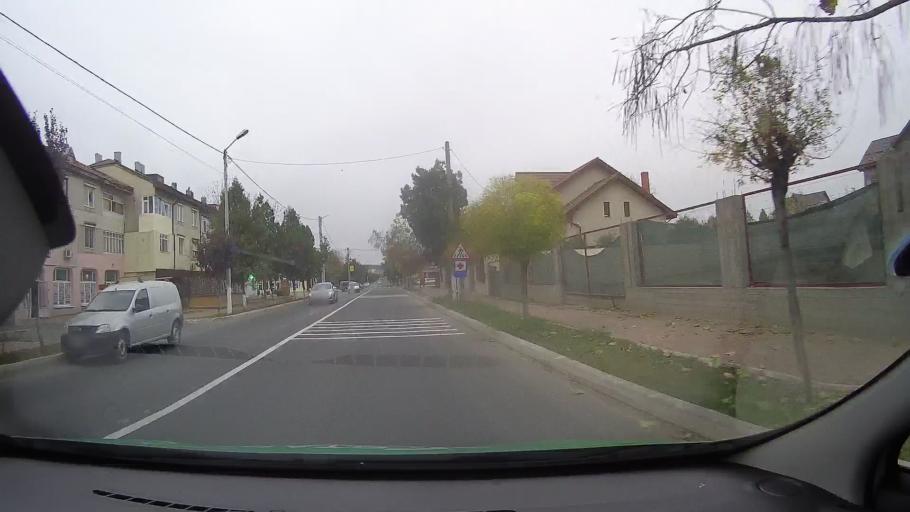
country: RO
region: Constanta
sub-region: Oras Harsova
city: Harsova
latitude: 44.6877
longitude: 27.9521
